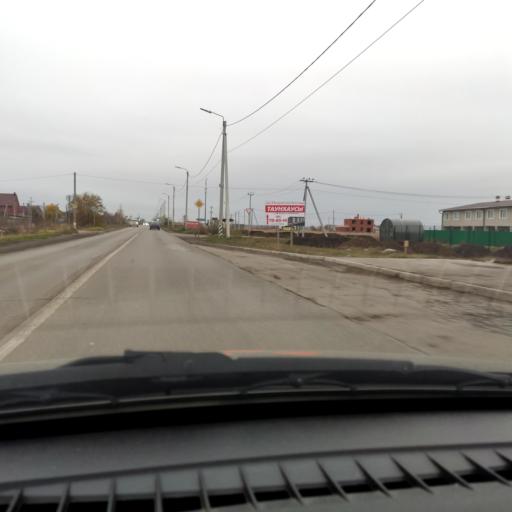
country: RU
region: Samara
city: Podstepki
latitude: 53.5217
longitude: 49.1885
